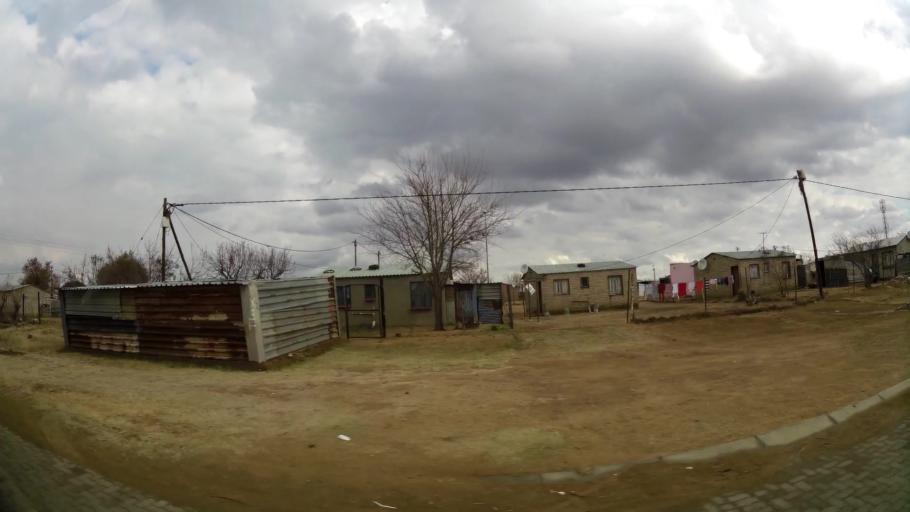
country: ZA
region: Orange Free State
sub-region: Fezile Dabi District Municipality
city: Sasolburg
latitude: -26.8785
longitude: 27.8773
